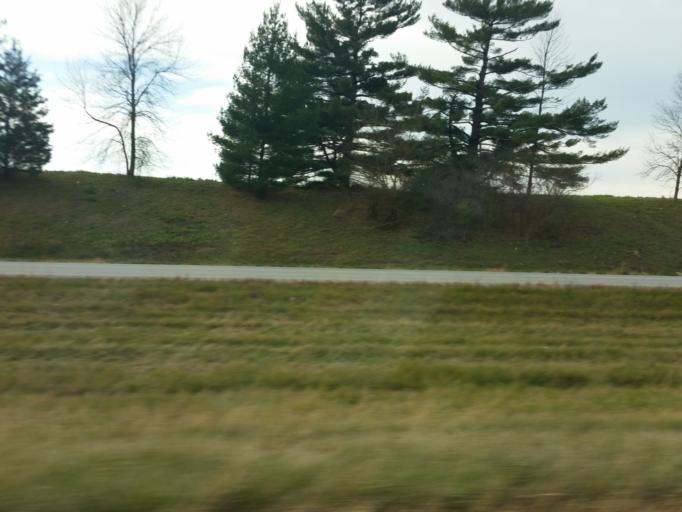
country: US
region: Illinois
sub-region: Henry County
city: Green Rock
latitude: 41.4504
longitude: -90.3710
